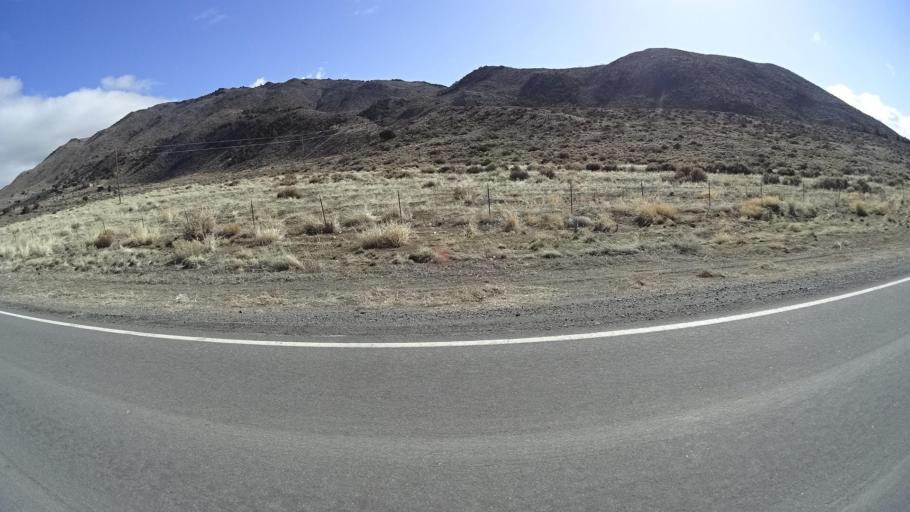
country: US
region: Nevada
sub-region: Washoe County
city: Cold Springs
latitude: 39.7544
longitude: -119.8859
